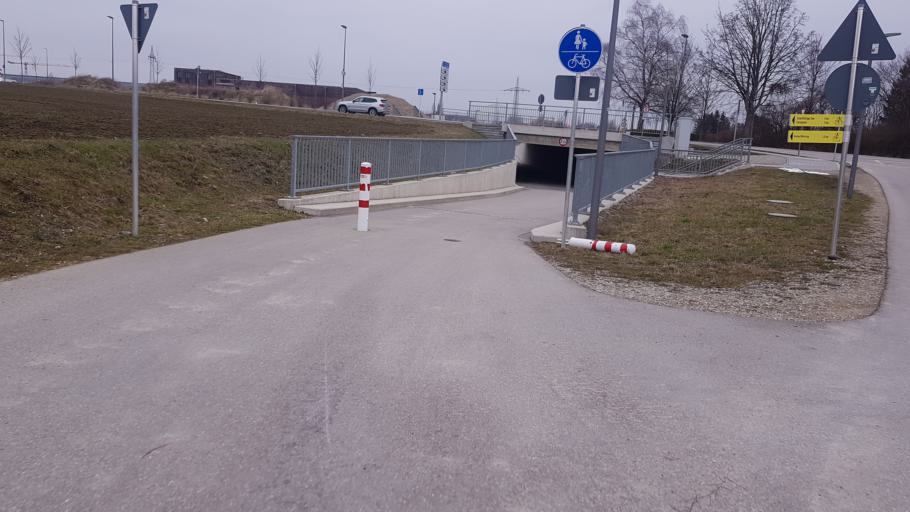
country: DE
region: Bavaria
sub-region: Upper Bavaria
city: Unterfoehring
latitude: 48.1810
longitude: 11.6534
